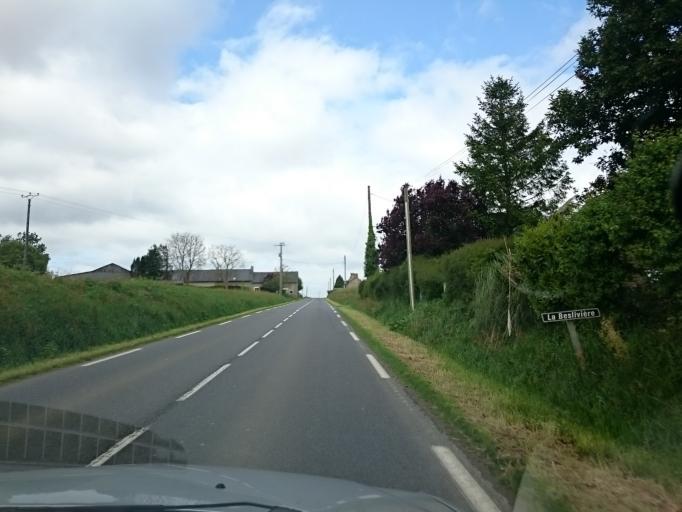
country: FR
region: Lower Normandy
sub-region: Departement de la Manche
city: Saint-James
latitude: 48.5364
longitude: -1.3563
